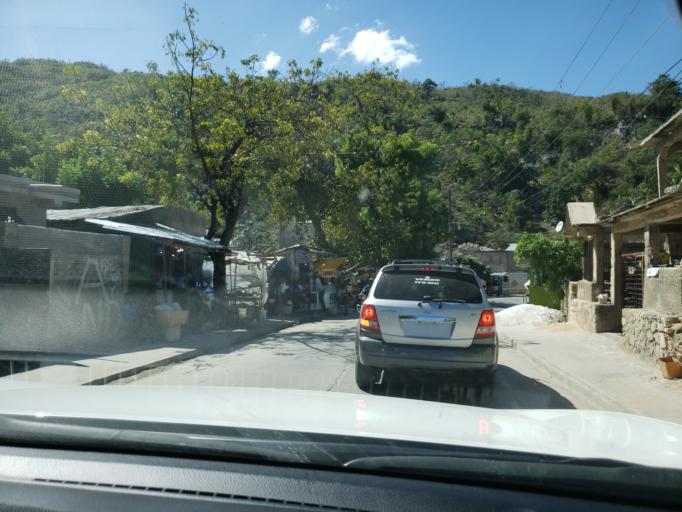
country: HT
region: Nippes
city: Miragoane
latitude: 18.4436
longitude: -73.0974
